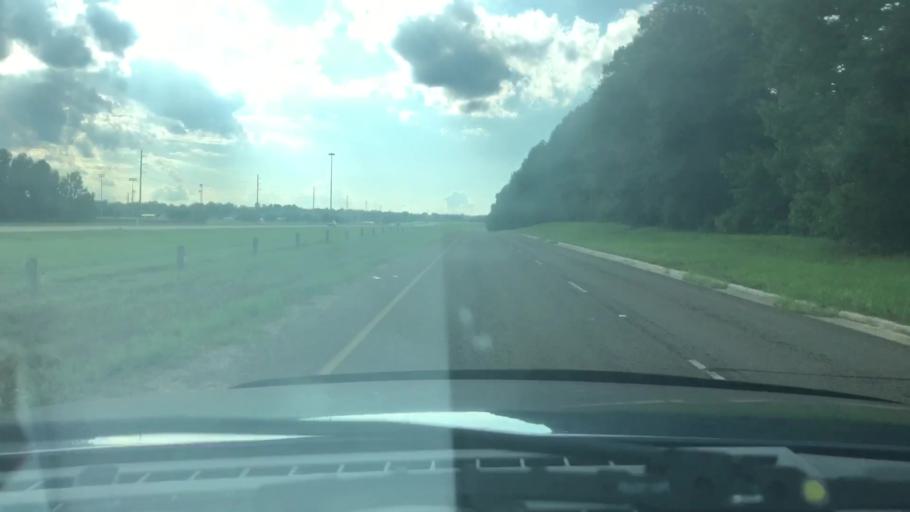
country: US
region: Texas
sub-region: Bowie County
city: Texarkana
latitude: 33.3865
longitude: -94.0779
